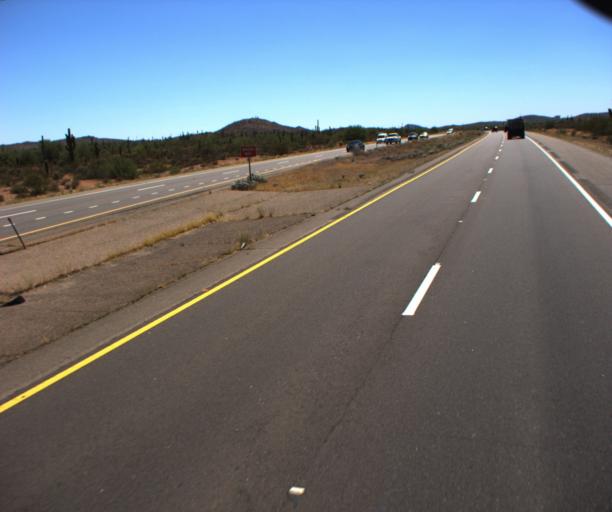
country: US
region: Arizona
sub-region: Maricopa County
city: Fountain Hills
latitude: 33.5778
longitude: -111.6867
